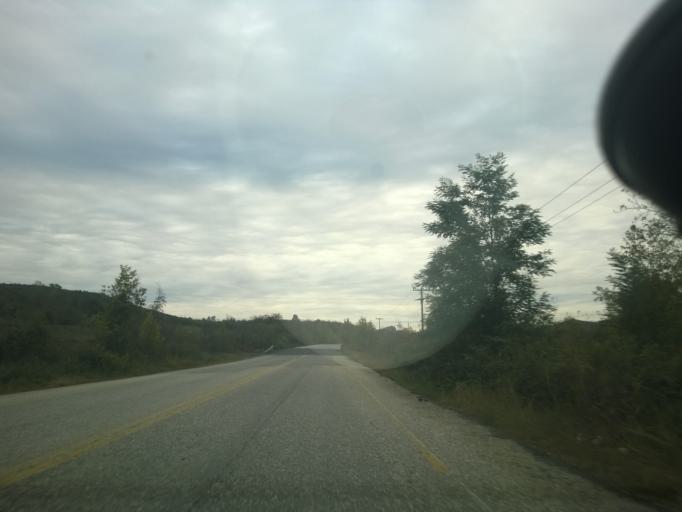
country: GR
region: Central Macedonia
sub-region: Nomos Pellis
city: Apsalos
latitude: 40.8566
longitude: 22.1050
